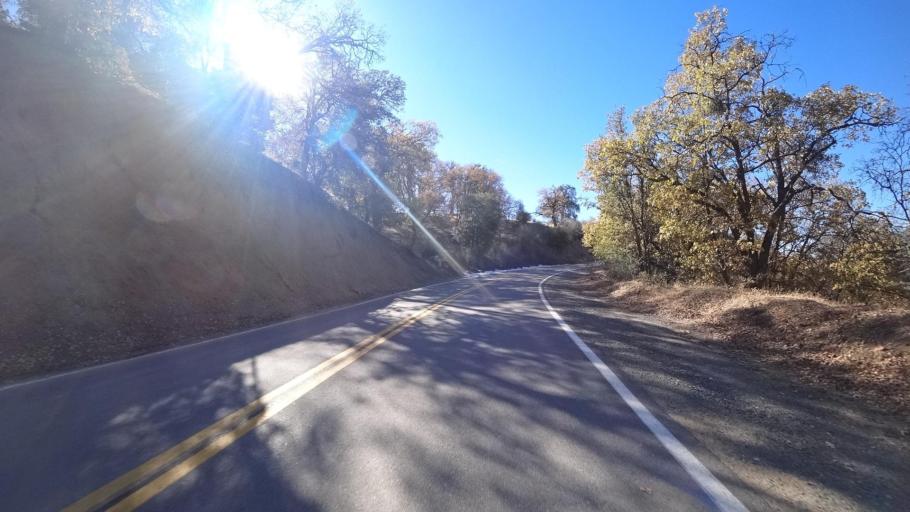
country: US
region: California
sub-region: Kern County
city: Alta Sierra
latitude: 35.7381
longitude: -118.6193
